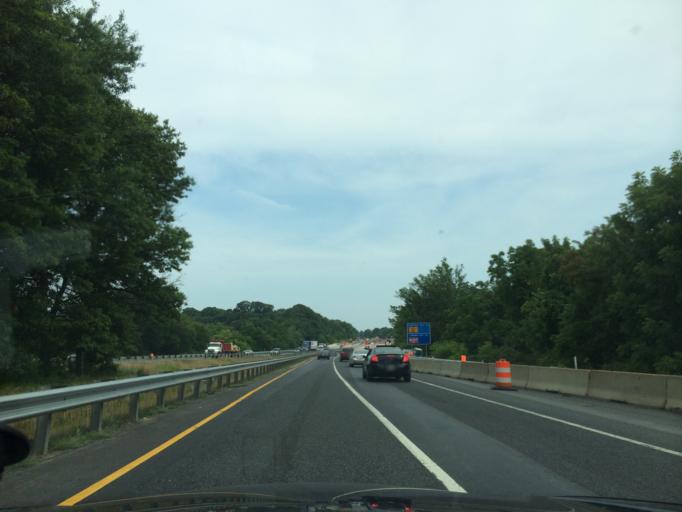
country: US
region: Maryland
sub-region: Washington County
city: Wilson-Conococheague
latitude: 39.6438
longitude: -77.8328
